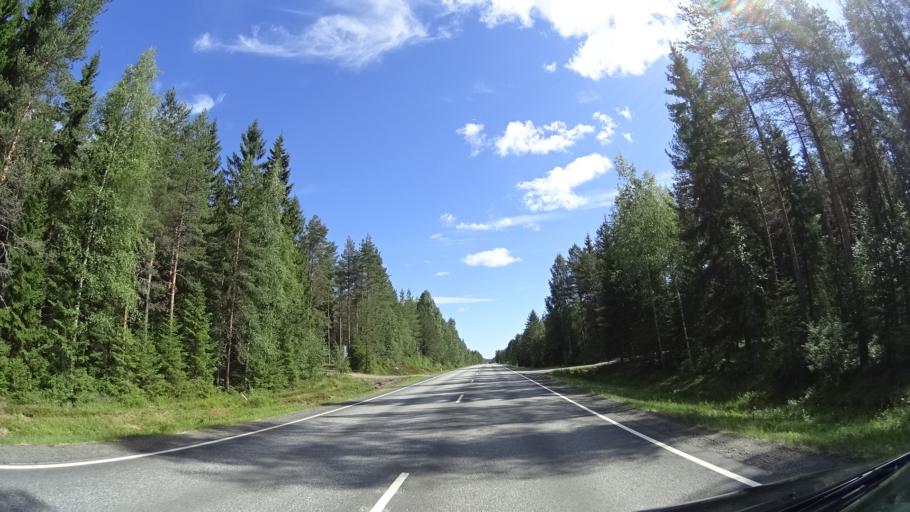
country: FI
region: Pirkanmaa
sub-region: Luoteis-Pirkanmaa
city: Kihnioe
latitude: 62.2045
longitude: 23.2262
